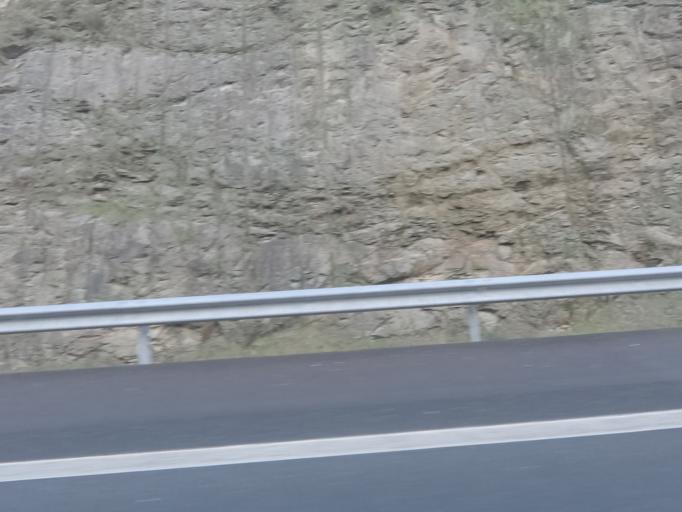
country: ES
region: Galicia
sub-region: Provincia da Coruna
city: Ribeira
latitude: 42.7400
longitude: -8.3702
